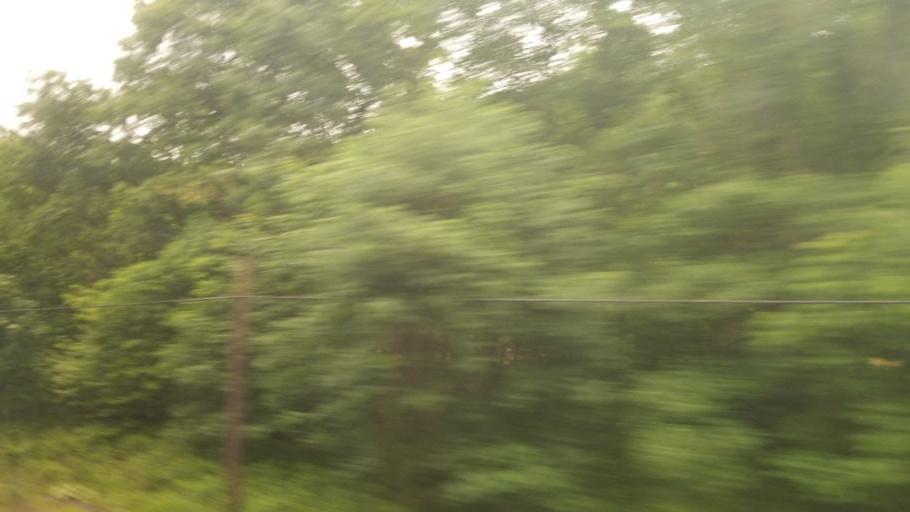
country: US
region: Pennsylvania
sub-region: Somerset County
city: Milford
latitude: 39.8996
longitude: -79.1955
